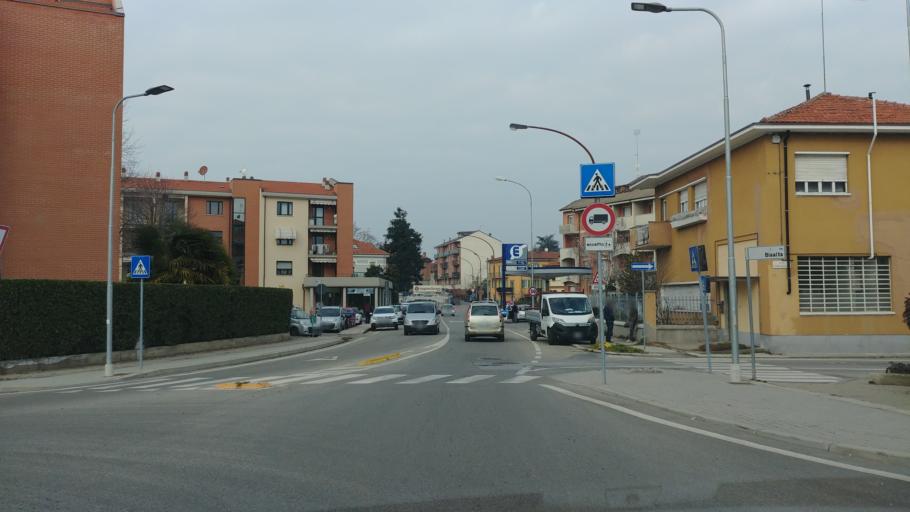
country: IT
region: Piedmont
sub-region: Provincia di Cuneo
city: Fossano
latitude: 44.5431
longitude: 7.7209
